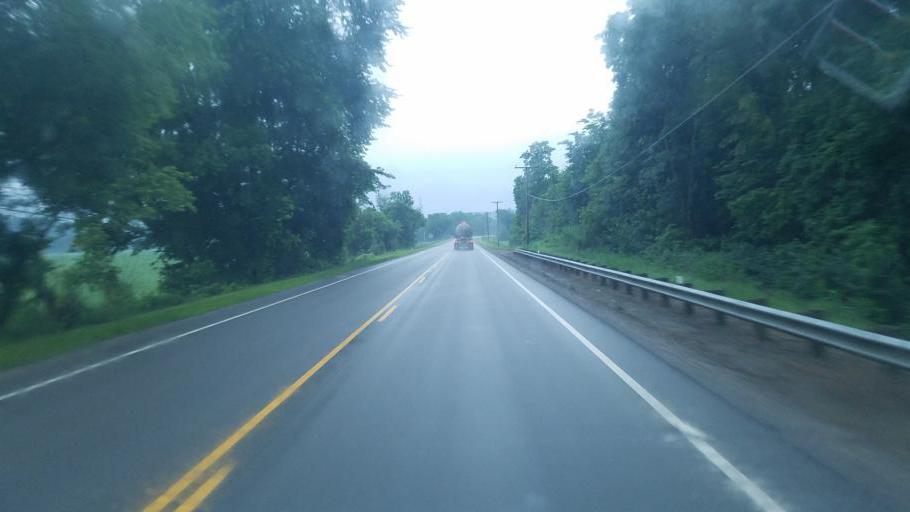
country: US
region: Ohio
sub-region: Coshocton County
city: Coshocton
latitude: 40.3261
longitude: -81.9417
